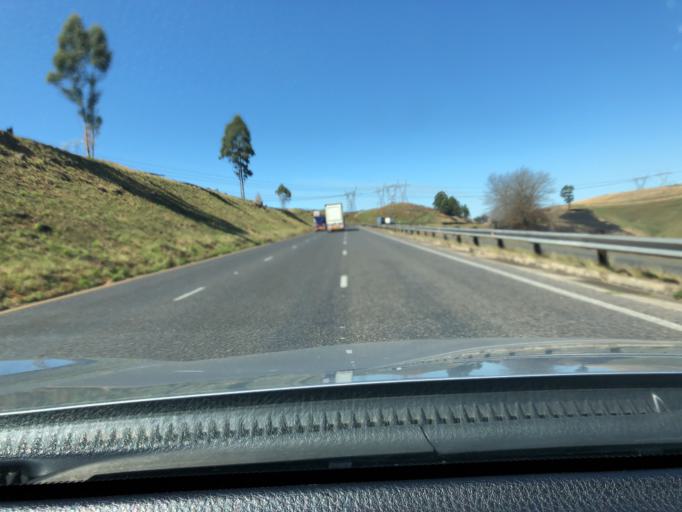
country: ZA
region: KwaZulu-Natal
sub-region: uMgungundlovu District Municipality
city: Howick
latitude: -29.4383
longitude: 30.1733
